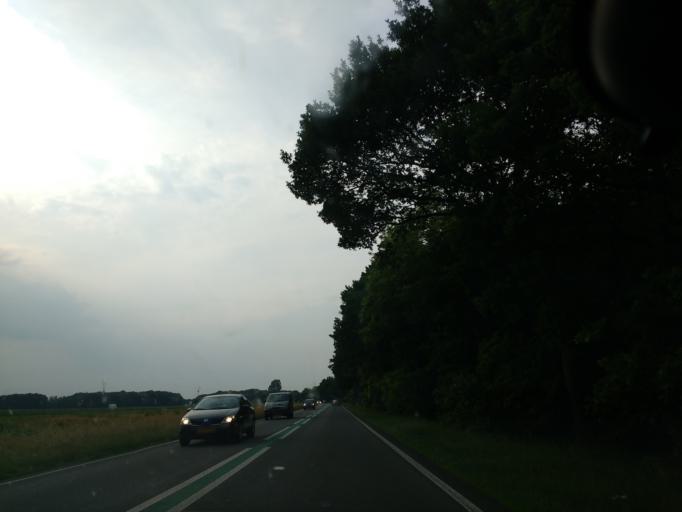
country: NL
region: Drenthe
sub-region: Gemeente Borger-Odoorn
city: Borger
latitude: 52.8964
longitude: 6.8160
